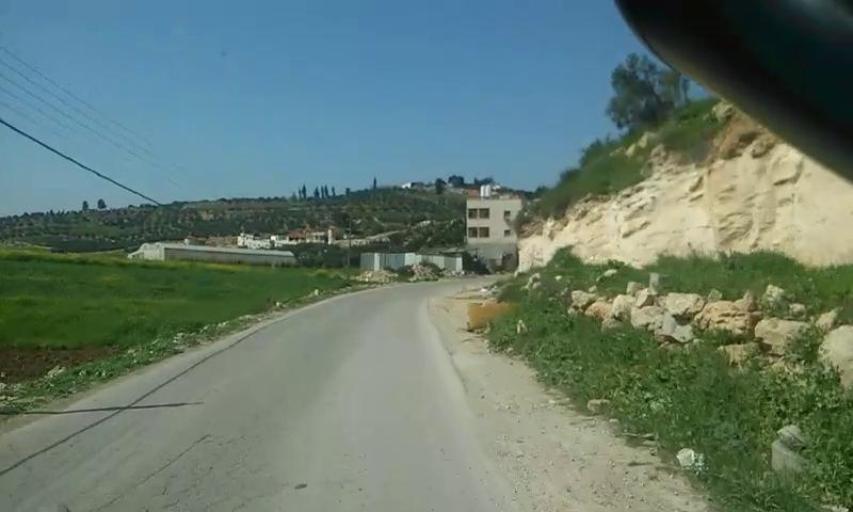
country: PS
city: Bayt Maqdum
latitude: 31.5458
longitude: 34.9639
